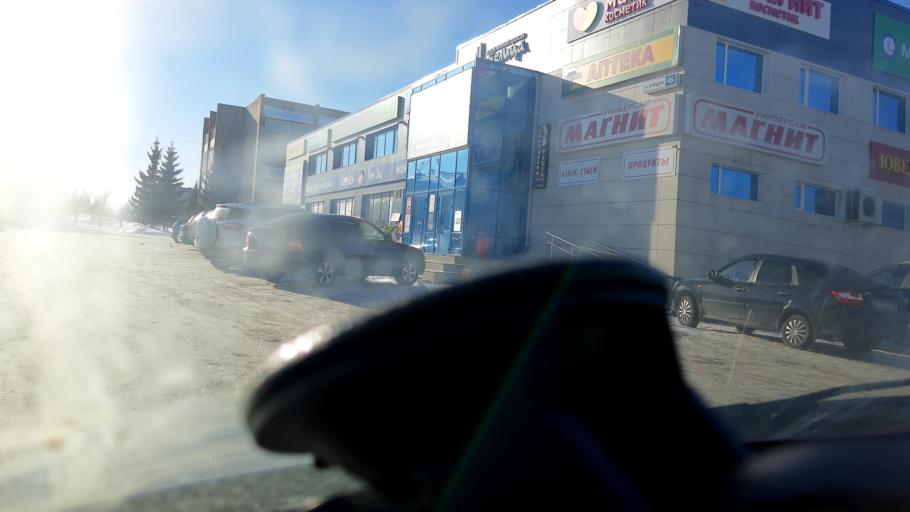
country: RU
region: Bashkortostan
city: Birsk
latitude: 55.4108
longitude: 55.5609
